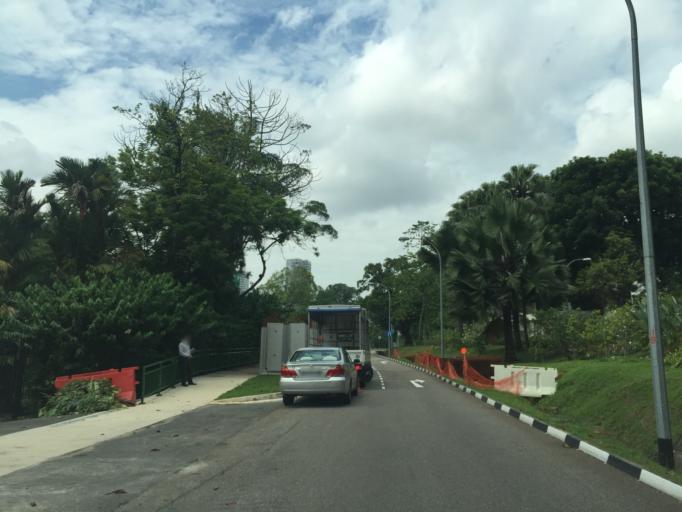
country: SG
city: Singapore
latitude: 1.3220
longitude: 103.8370
